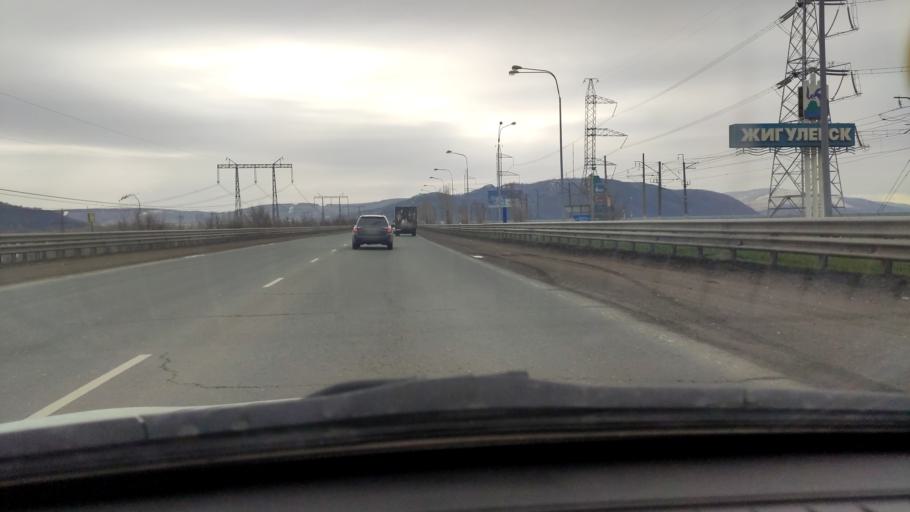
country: RU
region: Samara
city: Zhigulevsk
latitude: 53.4510
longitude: 49.4901
